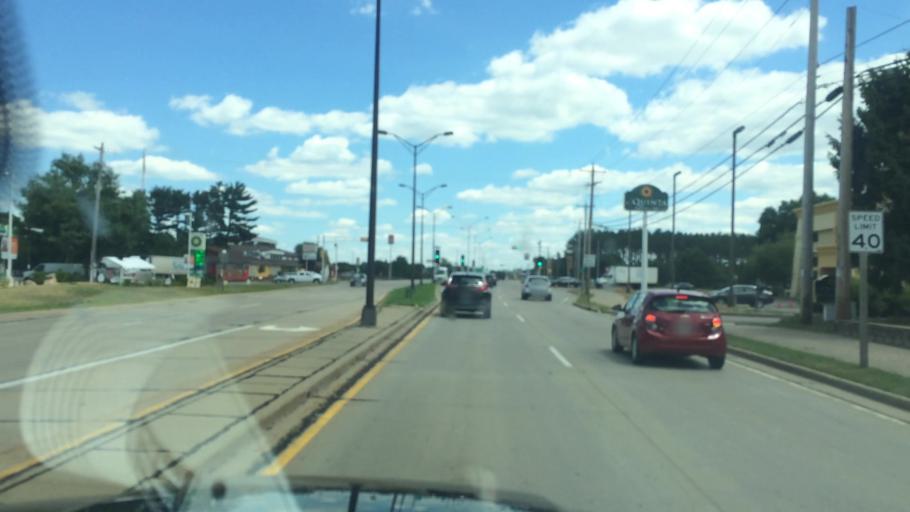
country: US
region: Wisconsin
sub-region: Portage County
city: Whiting
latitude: 44.5233
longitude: -89.5329
